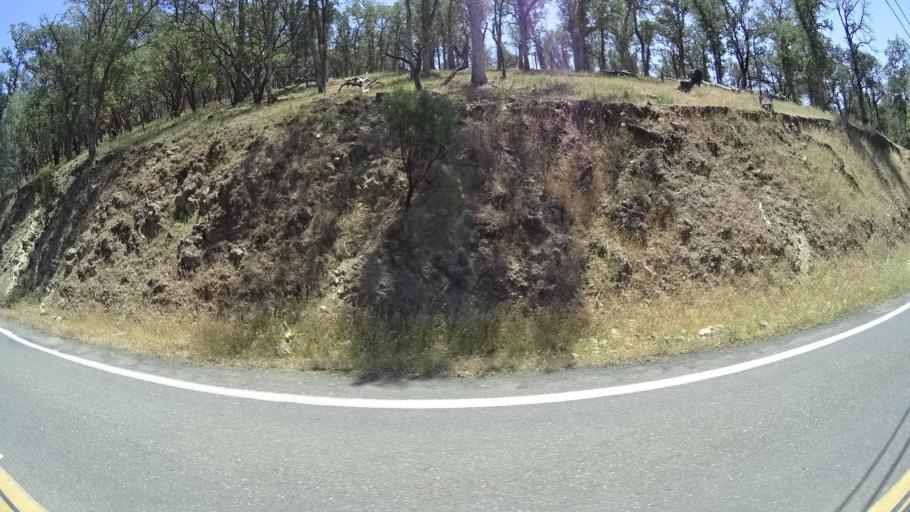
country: US
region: California
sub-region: Lake County
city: Hidden Valley Lake
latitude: 38.7992
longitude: -122.5470
